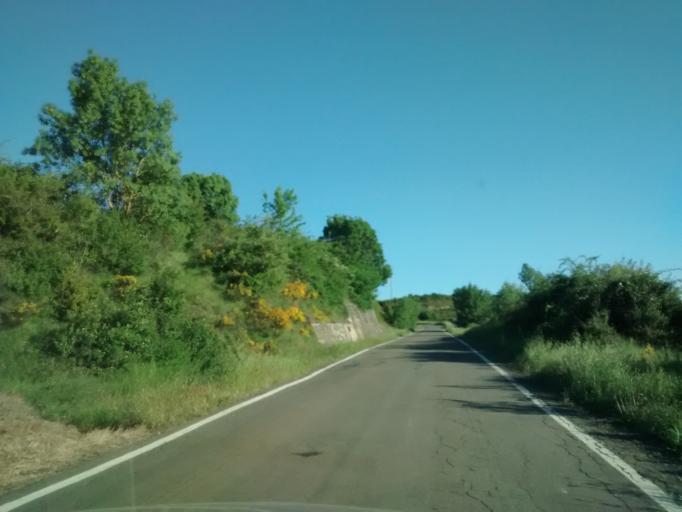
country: ES
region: Aragon
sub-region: Provincia de Huesca
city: Borau
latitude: 42.5961
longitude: -0.6140
